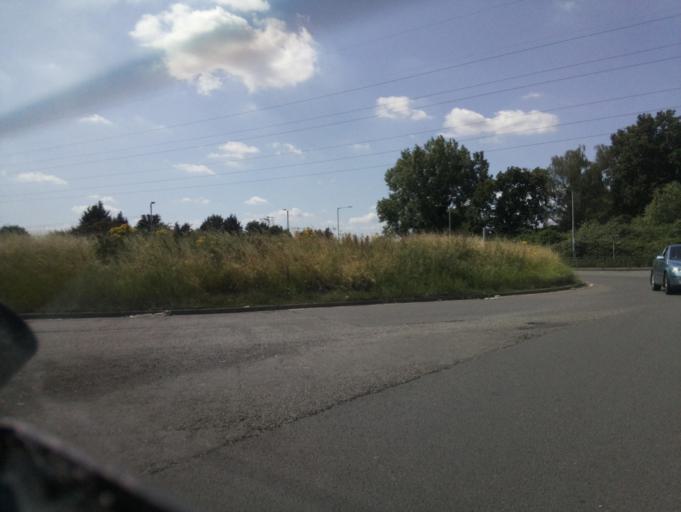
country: GB
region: England
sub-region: Leicestershire
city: Hinckley
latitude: 52.5285
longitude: -1.3967
